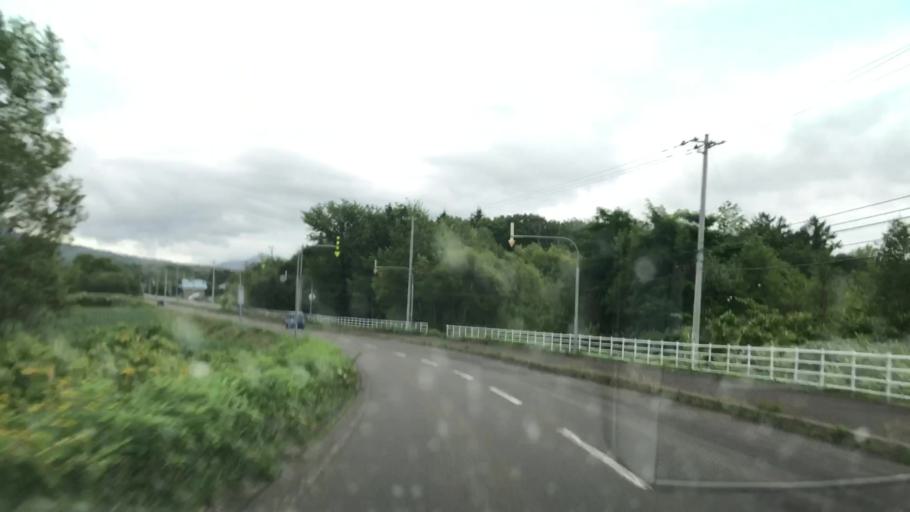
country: JP
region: Hokkaido
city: Niseko Town
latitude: 42.7953
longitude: 140.7149
